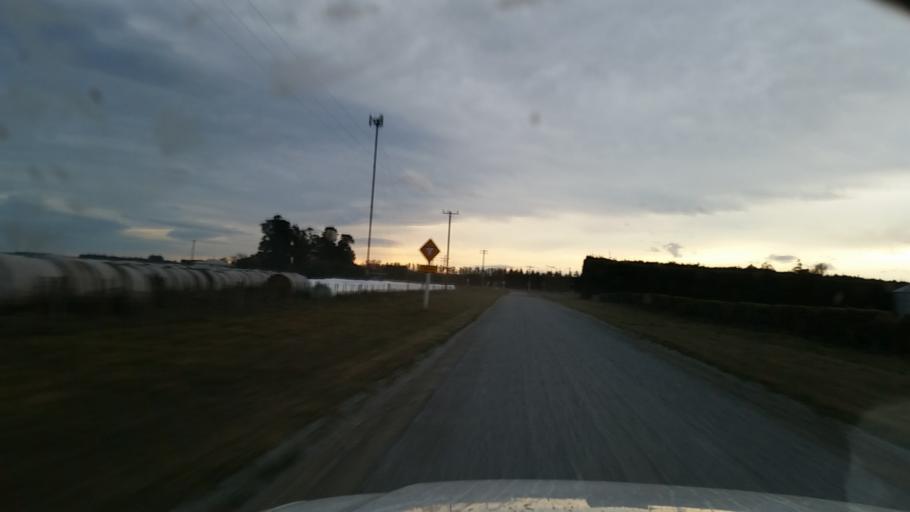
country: NZ
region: Canterbury
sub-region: Ashburton District
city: Tinwald
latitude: -43.8357
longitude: 171.6166
